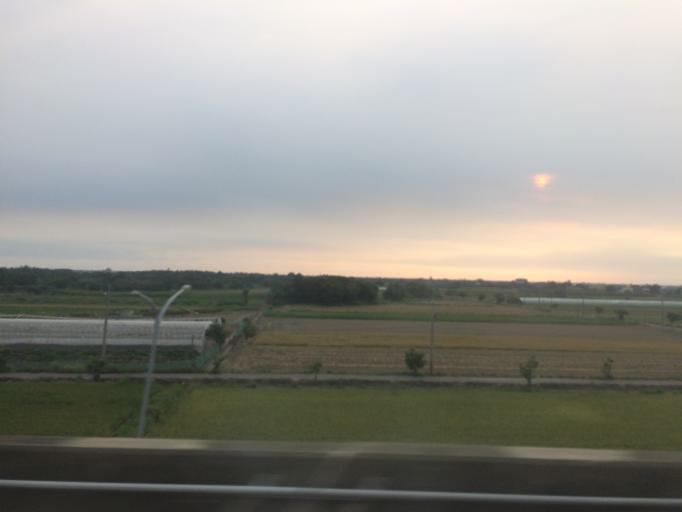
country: TW
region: Taiwan
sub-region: Chiayi
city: Taibao
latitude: 23.5093
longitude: 120.3262
